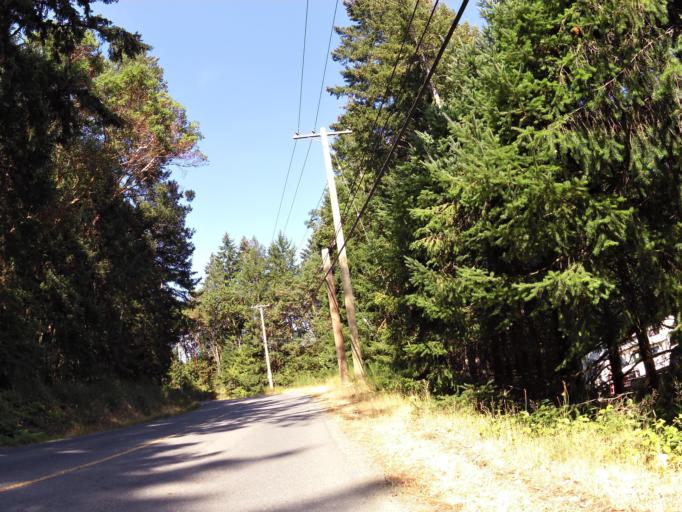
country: CA
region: British Columbia
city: North Saanich
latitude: 48.6719
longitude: -123.5528
